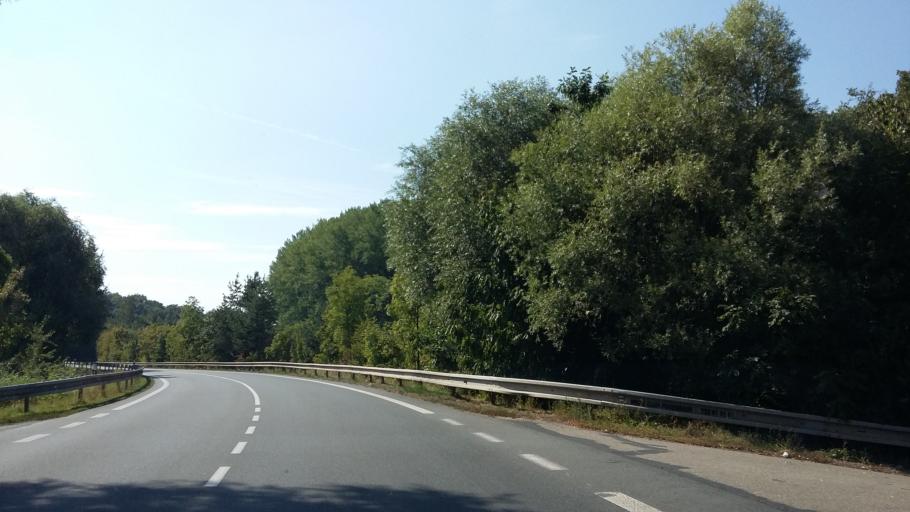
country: CZ
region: Central Bohemia
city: Libice nad Cidlinou
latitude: 50.1215
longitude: 15.1797
